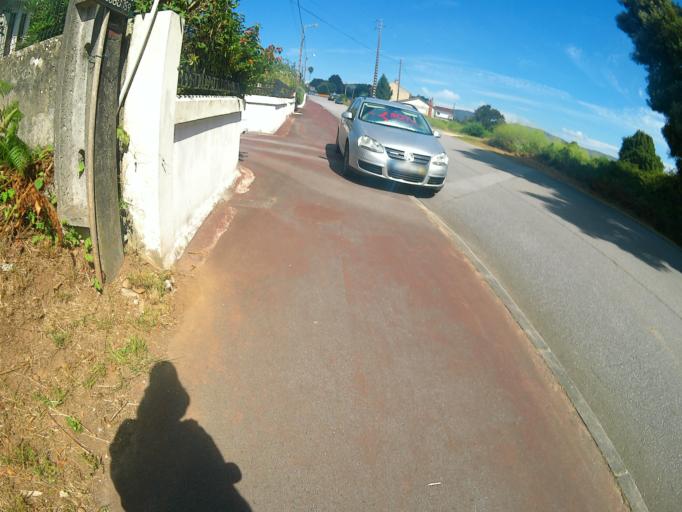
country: PT
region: Viana do Castelo
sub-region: Valenca
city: Valenca
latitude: 42.0254
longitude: -8.6525
